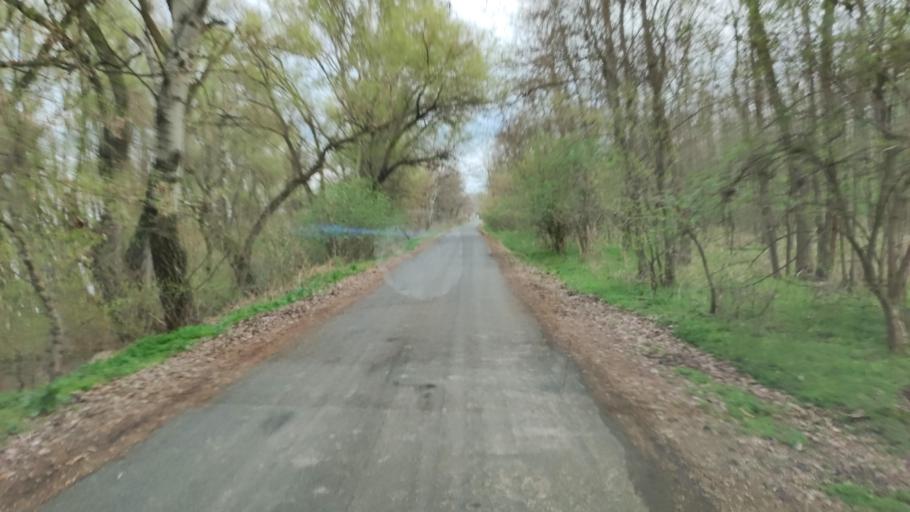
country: HU
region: Pest
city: Szigetujfalu
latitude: 47.2423
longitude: 18.9144
